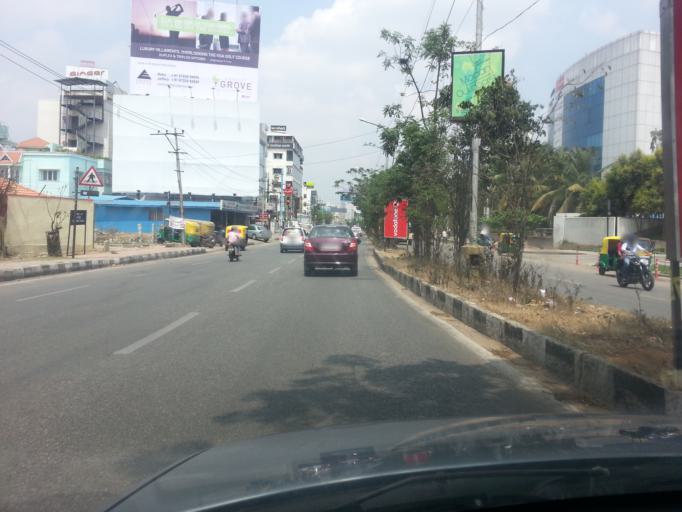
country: IN
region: Karnataka
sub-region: Bangalore Urban
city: Bangalore
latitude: 12.9513
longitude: 77.6396
